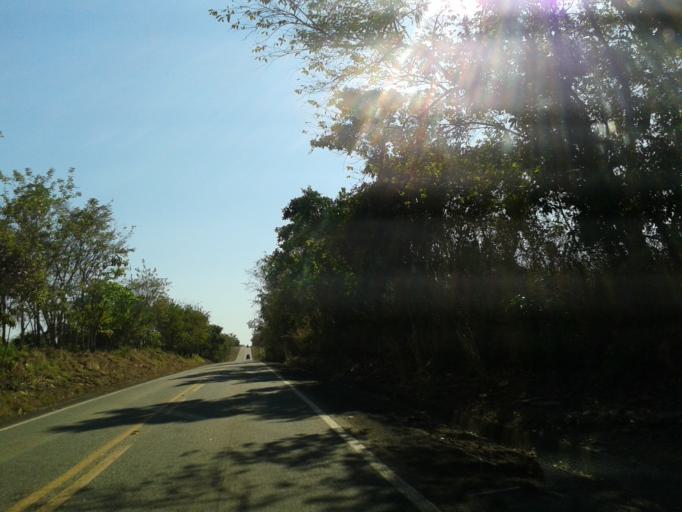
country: BR
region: Goias
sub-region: Mozarlandia
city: Mozarlandia
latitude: -14.5690
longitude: -50.5001
